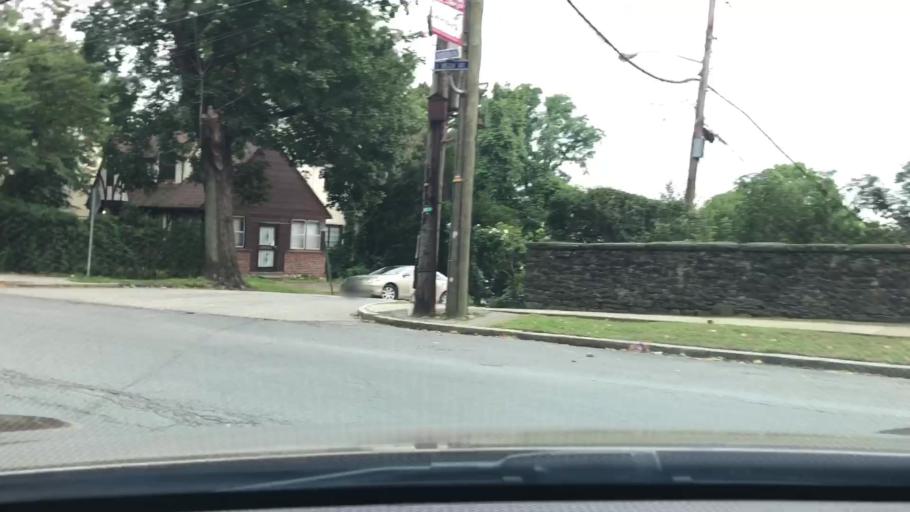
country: US
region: New York
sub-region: Westchester County
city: Pelham
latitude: 40.9180
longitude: -73.8205
